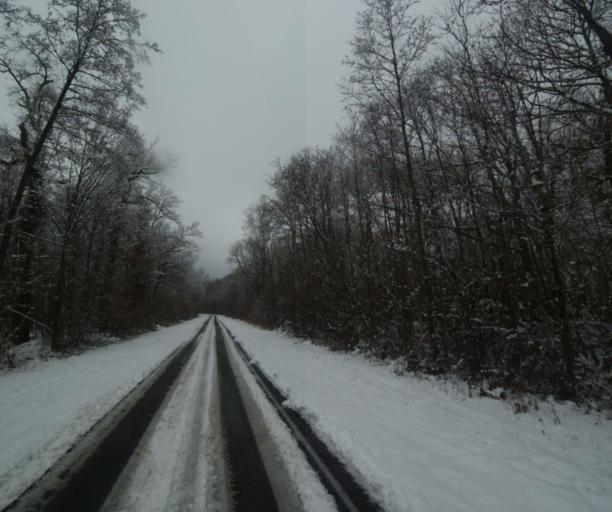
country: FR
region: Champagne-Ardenne
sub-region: Departement de la Haute-Marne
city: Wassy
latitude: 48.4652
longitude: 4.9453
